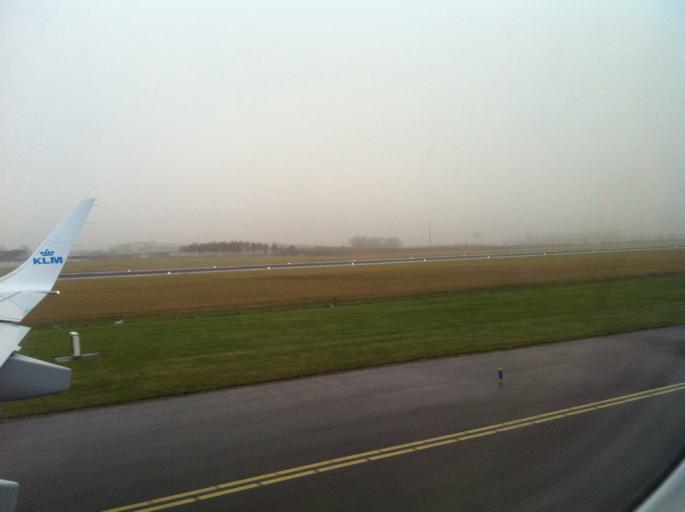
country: NL
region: North Holland
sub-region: Gemeente Aalsmeer
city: Aalsmeer
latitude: 52.3152
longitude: 4.7555
